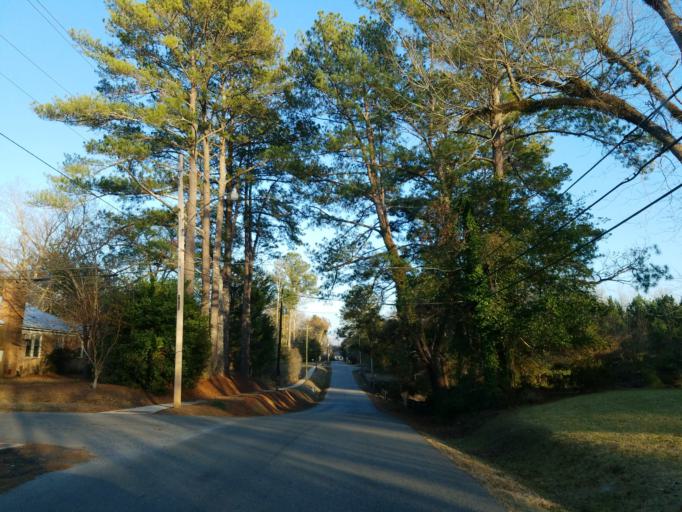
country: US
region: Mississippi
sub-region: Clarke County
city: Stonewall
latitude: 32.1743
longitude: -88.8247
